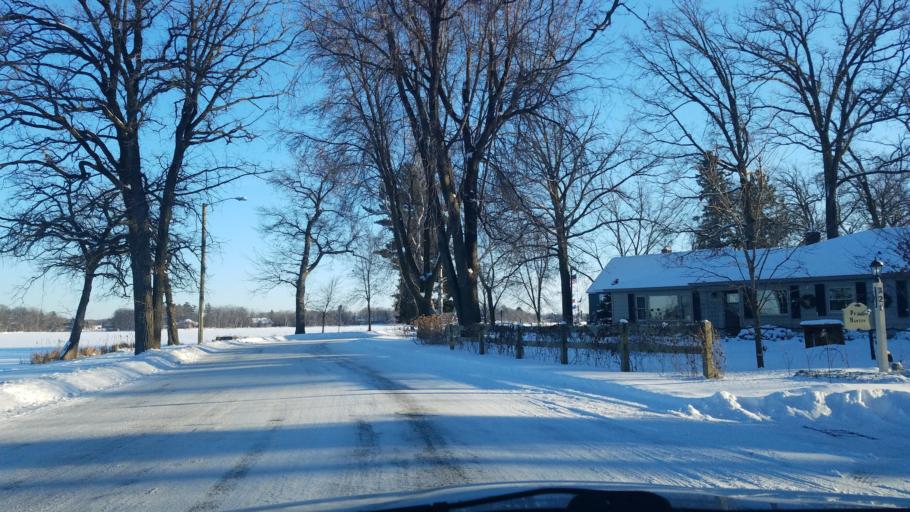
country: US
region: Wisconsin
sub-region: Barron County
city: Rice Lake
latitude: 45.5052
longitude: -91.7314
